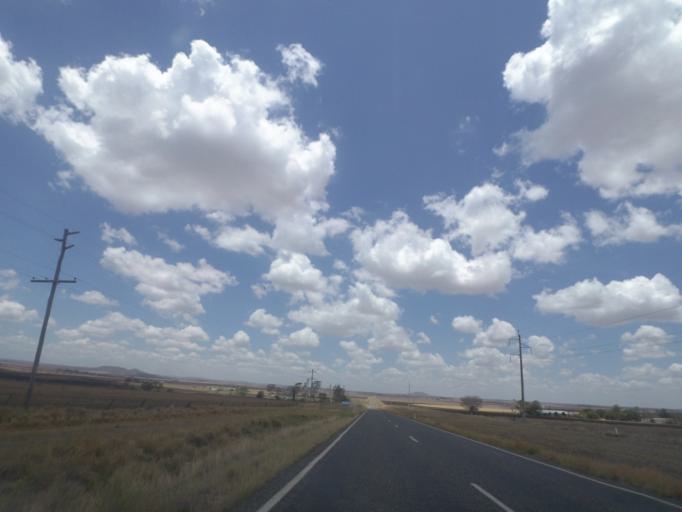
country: AU
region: Queensland
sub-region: Toowoomba
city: Top Camp
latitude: -27.8900
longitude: 151.9728
